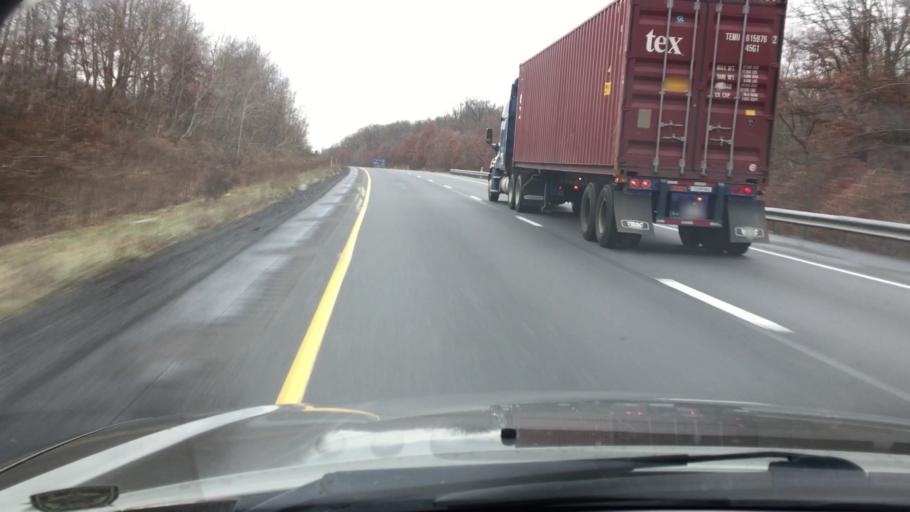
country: US
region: Pennsylvania
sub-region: Luzerne County
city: Freeland
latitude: 41.0589
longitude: -75.9393
